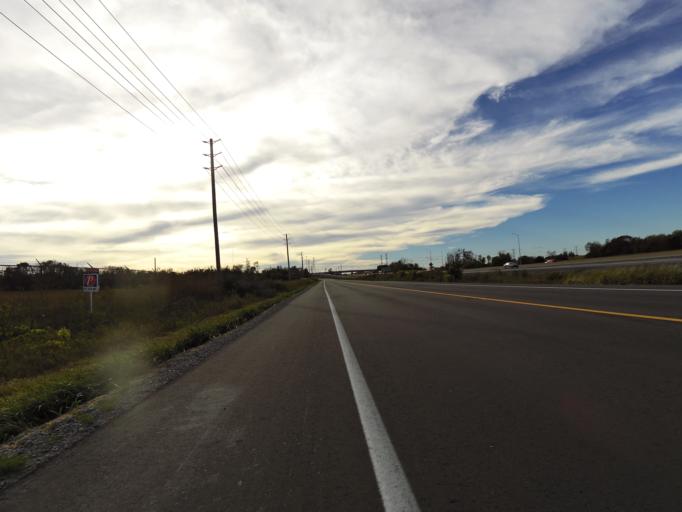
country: CA
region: Ontario
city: Oshawa
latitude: 43.8846
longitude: -78.7141
